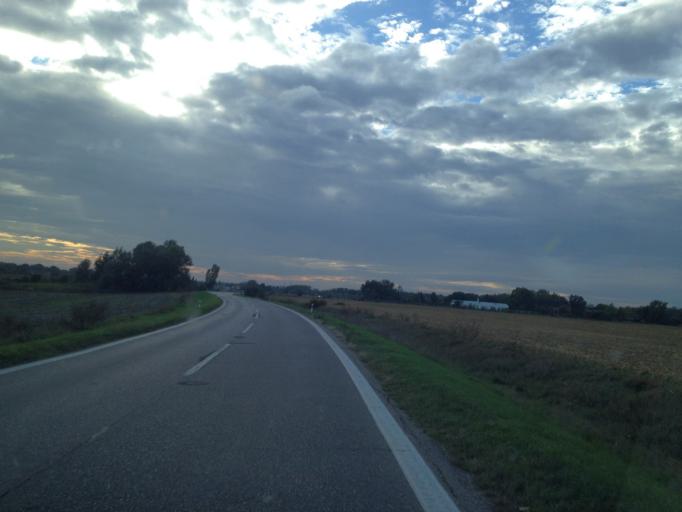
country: SK
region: Nitriansky
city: Komarno
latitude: 47.7654
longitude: 18.1709
